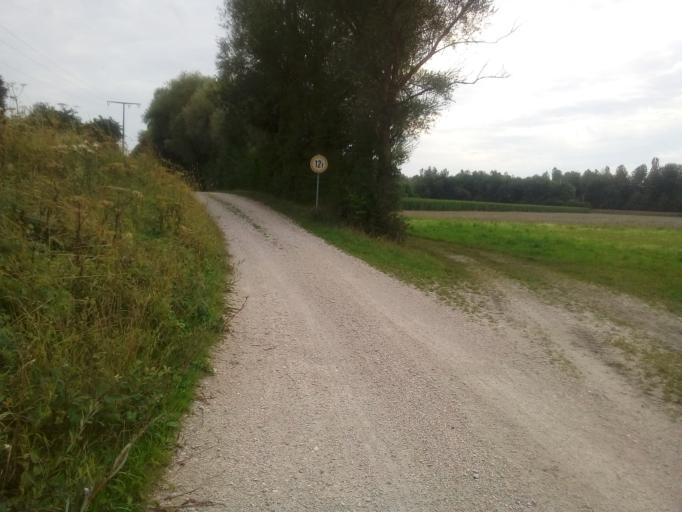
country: DE
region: Bavaria
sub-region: Upper Bavaria
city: Unterfoehring
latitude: 48.2059
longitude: 11.6699
